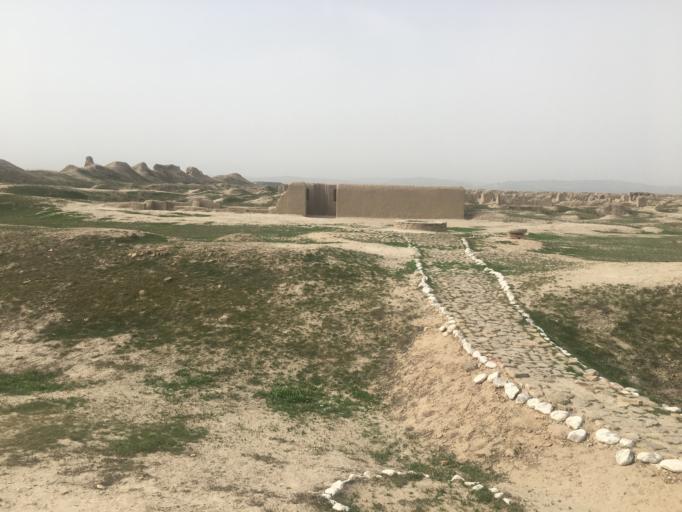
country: TM
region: Ahal
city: Kaka
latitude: 37.3932
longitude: 59.5661
